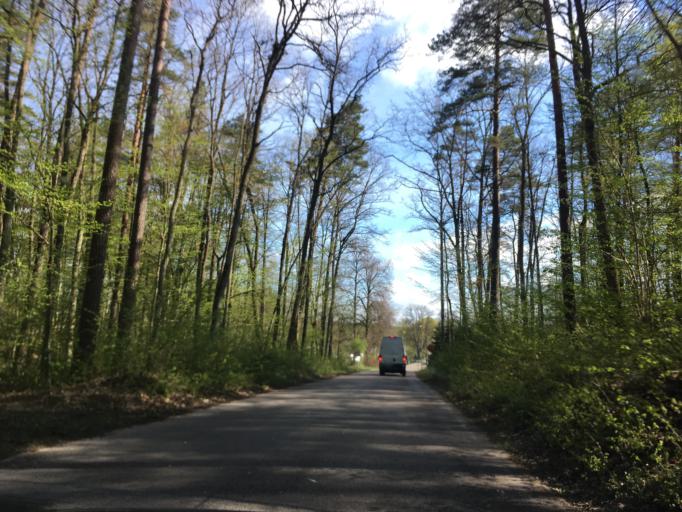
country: PL
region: Warmian-Masurian Voivodeship
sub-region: Powiat piski
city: Ruciane-Nida
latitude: 53.6579
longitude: 21.5630
